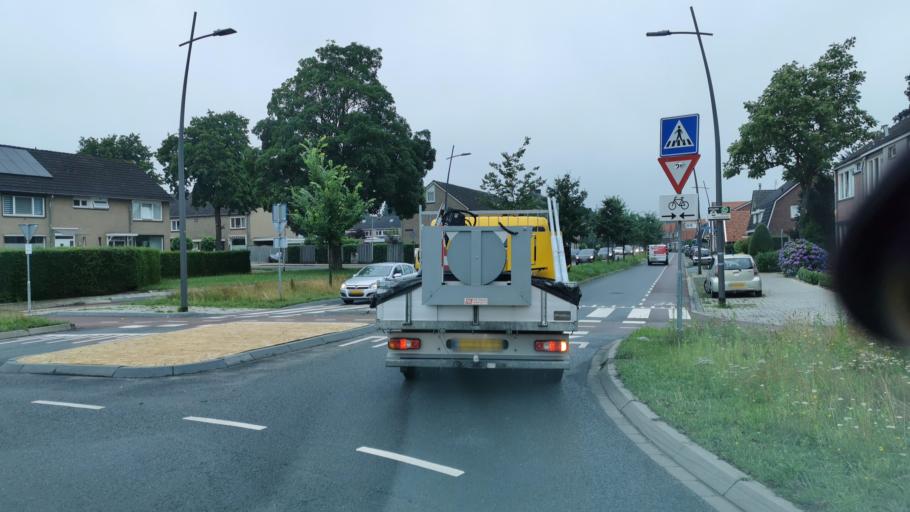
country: NL
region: Overijssel
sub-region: Gemeente Losser
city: Losser
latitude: 52.2517
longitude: 7.0097
